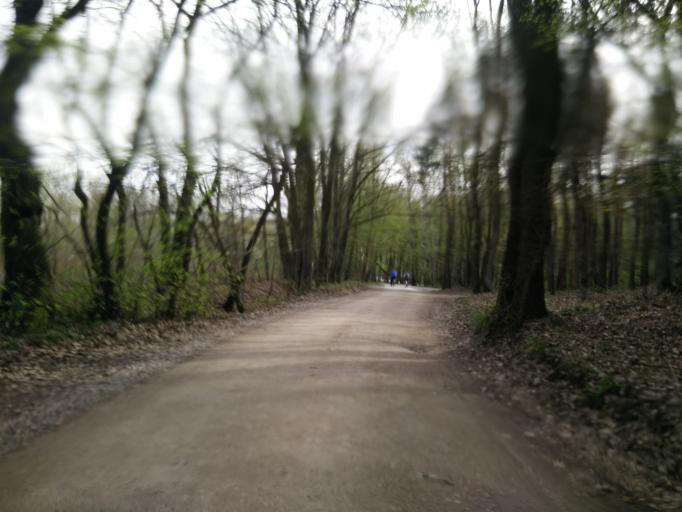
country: PL
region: Masovian Voivodeship
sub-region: Powiat warszawski zachodni
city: Stare Babice
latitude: 52.2838
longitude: 20.8415
